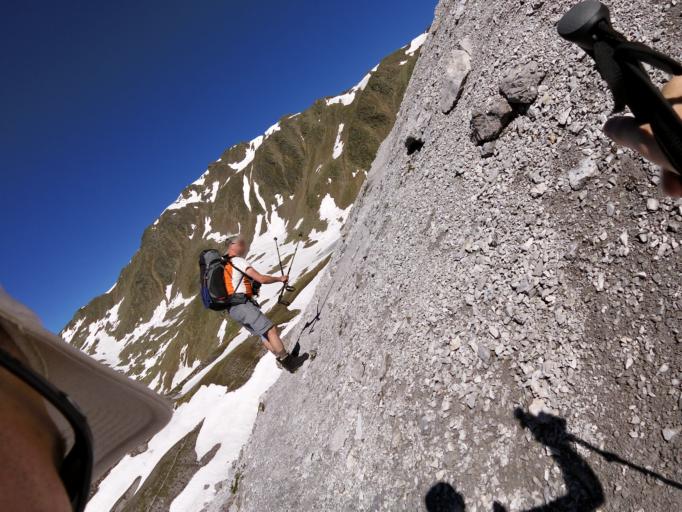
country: AT
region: Tyrol
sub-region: Politischer Bezirk Innsbruck Land
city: Neustift im Stubaital
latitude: 47.1422
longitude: 11.2715
